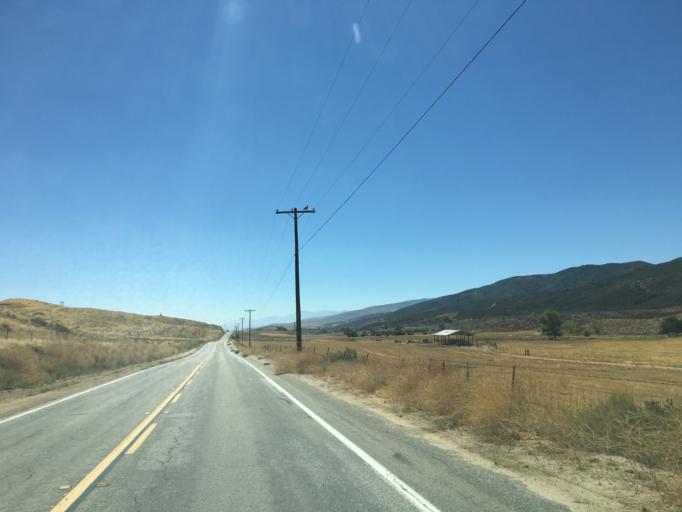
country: US
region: California
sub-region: Los Angeles County
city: Green Valley
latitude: 34.6419
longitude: -118.3591
